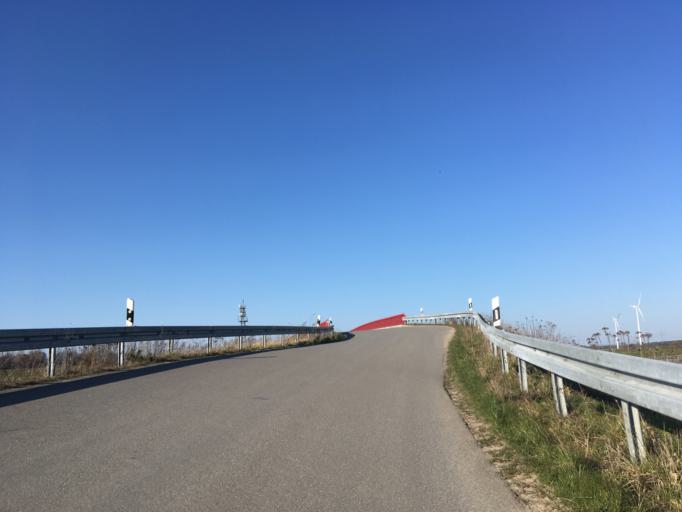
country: DE
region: Brandenburg
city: Ahrensfelde
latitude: 52.6109
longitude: 13.5692
